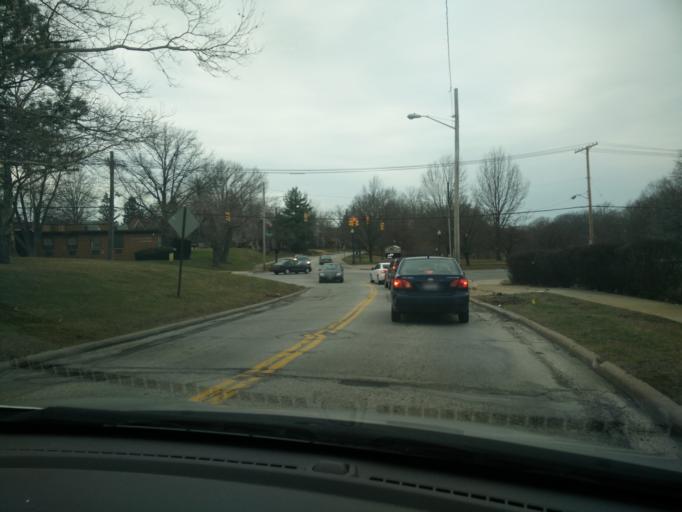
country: US
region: Ohio
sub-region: Cuyahoga County
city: Cleveland Heights
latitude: 41.5047
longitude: -81.5552
